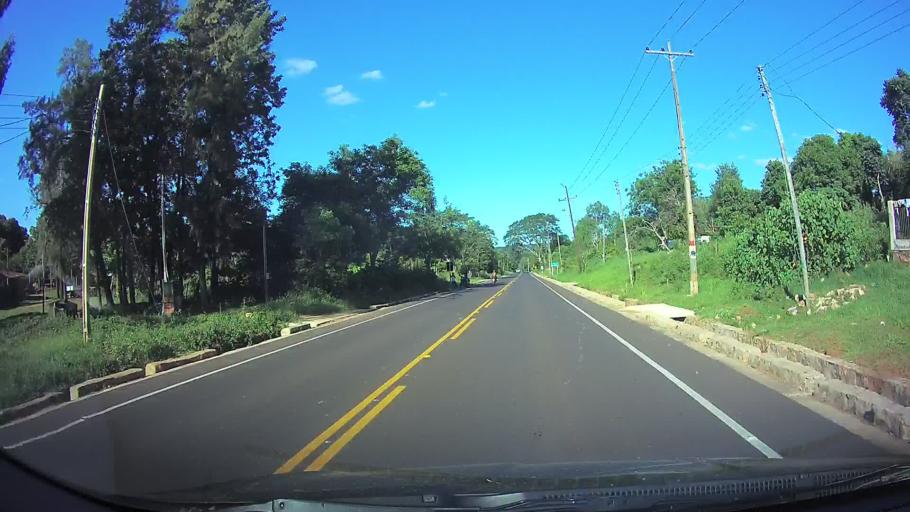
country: PY
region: Cordillera
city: Caacupe
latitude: -25.3242
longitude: -57.1548
